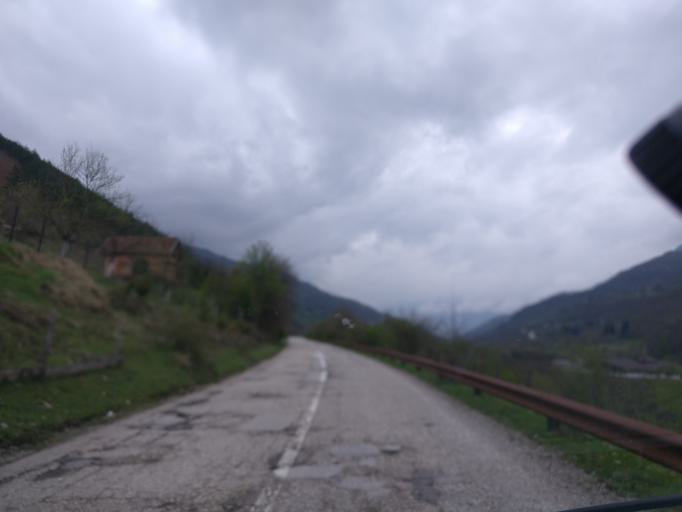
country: BA
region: Republika Srpska
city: Foca
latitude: 43.4458
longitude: 18.7563
